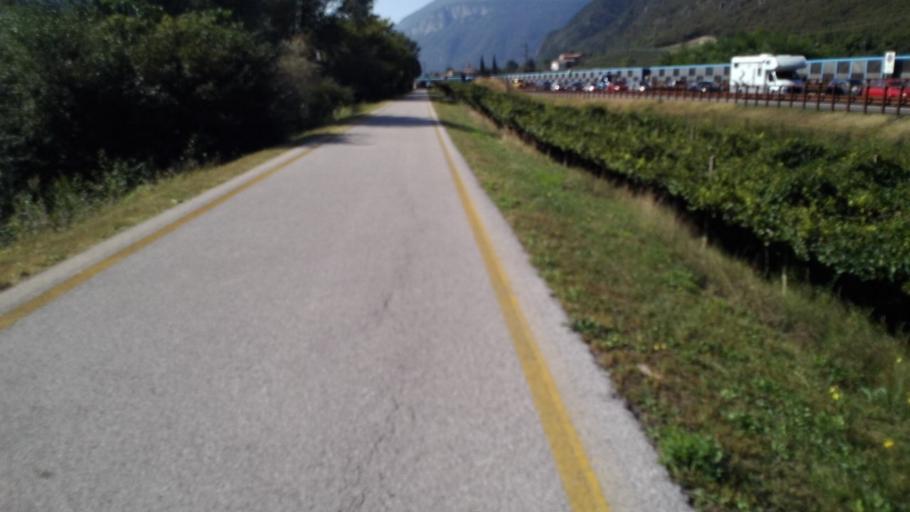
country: IT
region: Trentino-Alto Adige
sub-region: Provincia di Trento
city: Avio
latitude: 45.7114
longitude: 10.9288
